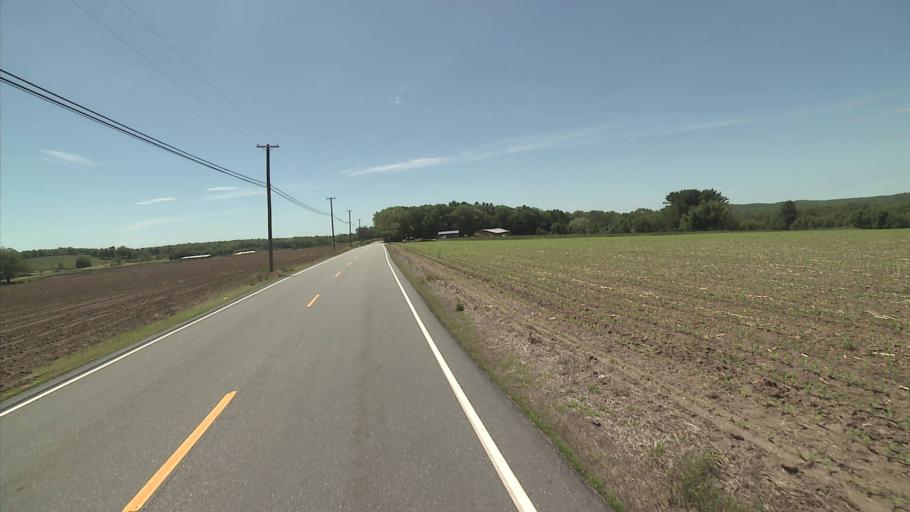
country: US
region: Rhode Island
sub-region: Washington County
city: Hopkinton
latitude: 41.5412
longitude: -71.8408
